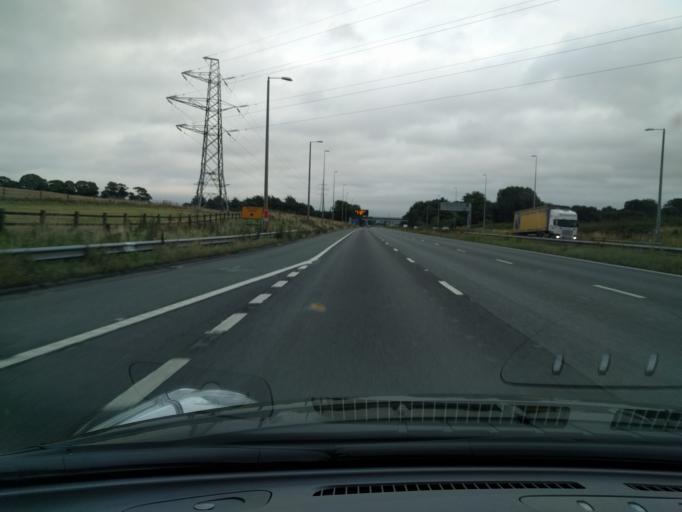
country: GB
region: England
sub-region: Warrington
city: Winwick
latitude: 53.4369
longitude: -2.5773
